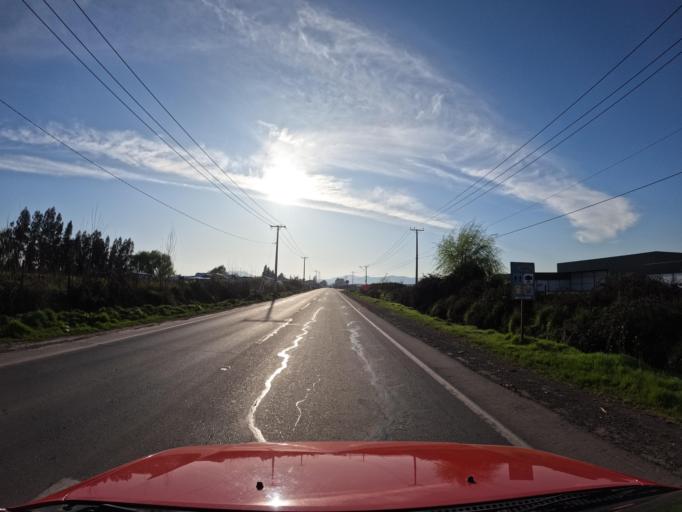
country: CL
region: Maule
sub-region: Provincia de Curico
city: Teno
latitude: -34.8542
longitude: -71.1072
